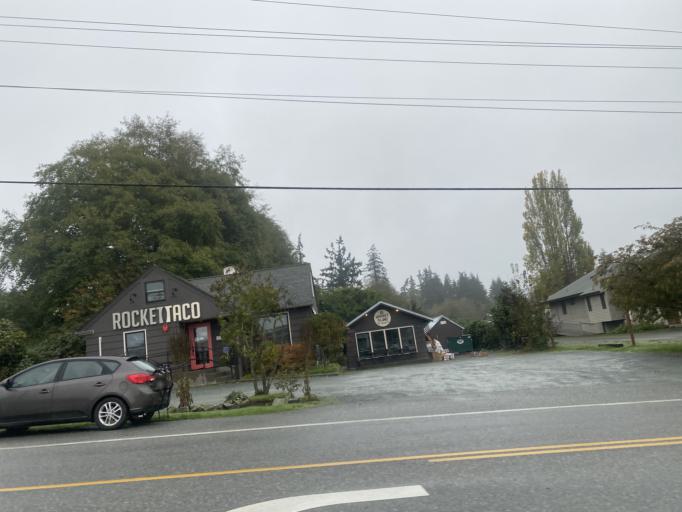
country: US
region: Washington
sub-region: Island County
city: Freeland
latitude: 48.0096
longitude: -122.5288
